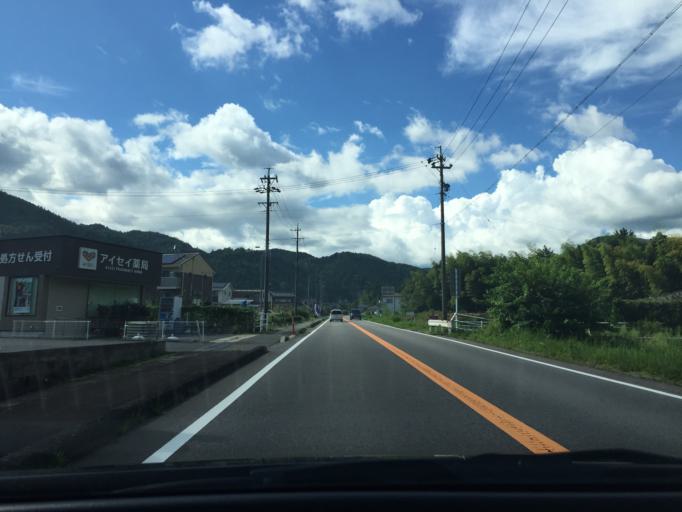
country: JP
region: Gifu
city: Nakatsugawa
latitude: 35.6698
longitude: 137.4202
